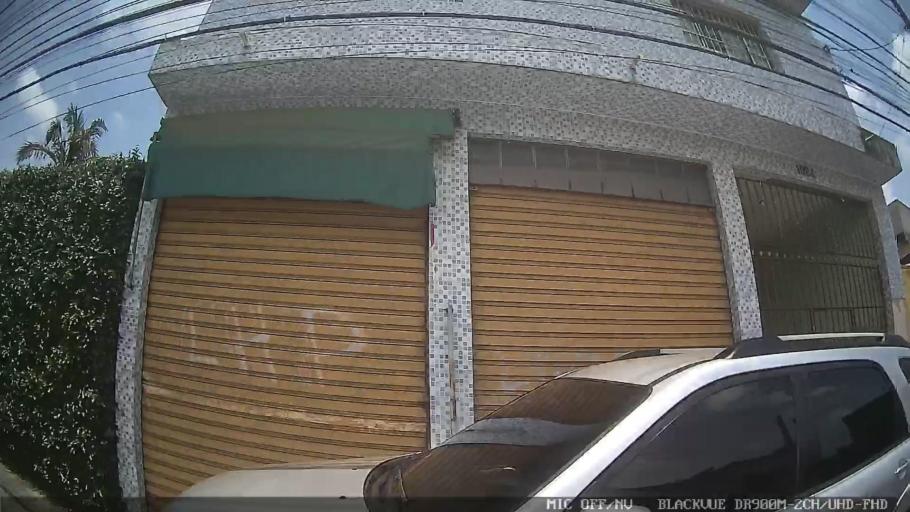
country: BR
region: Sao Paulo
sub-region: Ferraz De Vasconcelos
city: Ferraz de Vasconcelos
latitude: -23.5539
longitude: -46.3724
